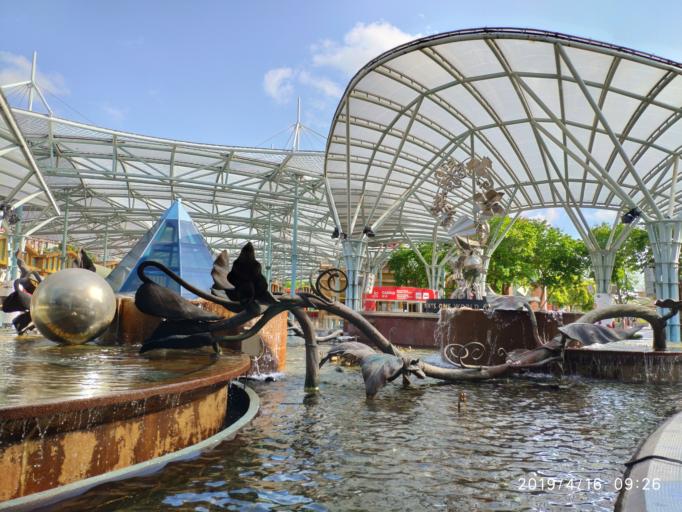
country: SG
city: Singapore
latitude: 1.2559
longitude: 103.8204
